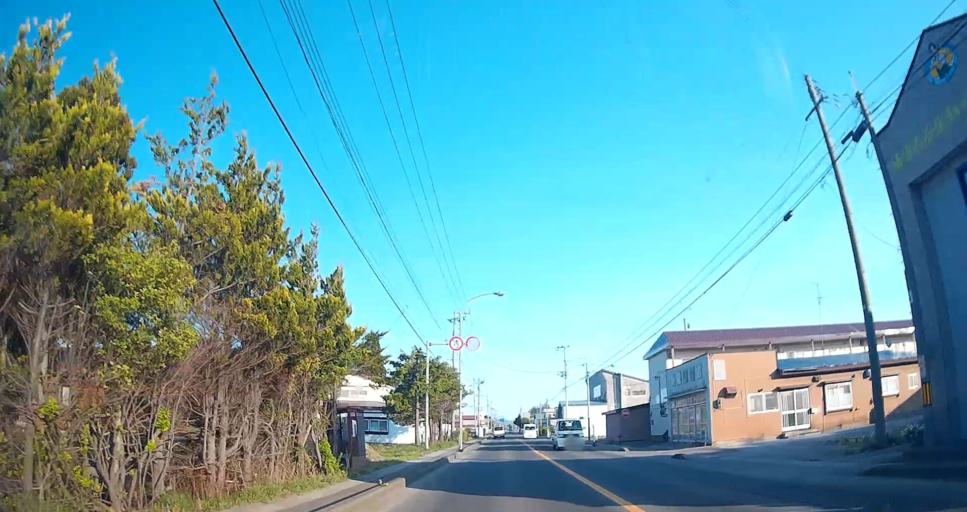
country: JP
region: Aomori
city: Mutsu
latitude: 41.2747
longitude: 141.2148
